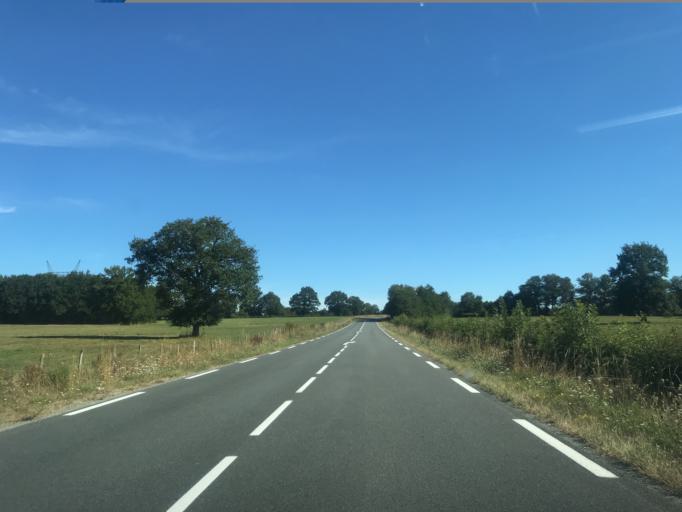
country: FR
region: Limousin
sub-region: Departement de la Creuse
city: Gouzon
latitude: 46.1538
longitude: 2.2095
